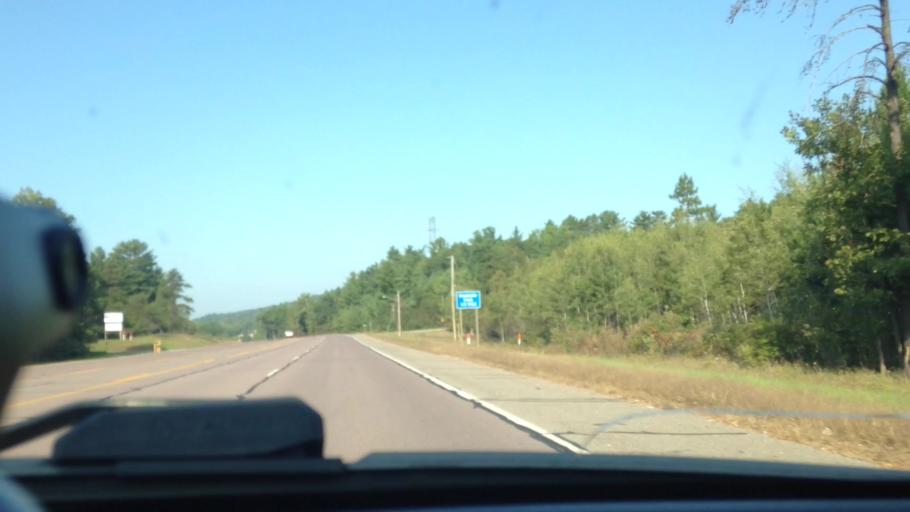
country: US
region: Michigan
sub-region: Dickinson County
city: Quinnesec
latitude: 45.8037
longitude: -87.9667
